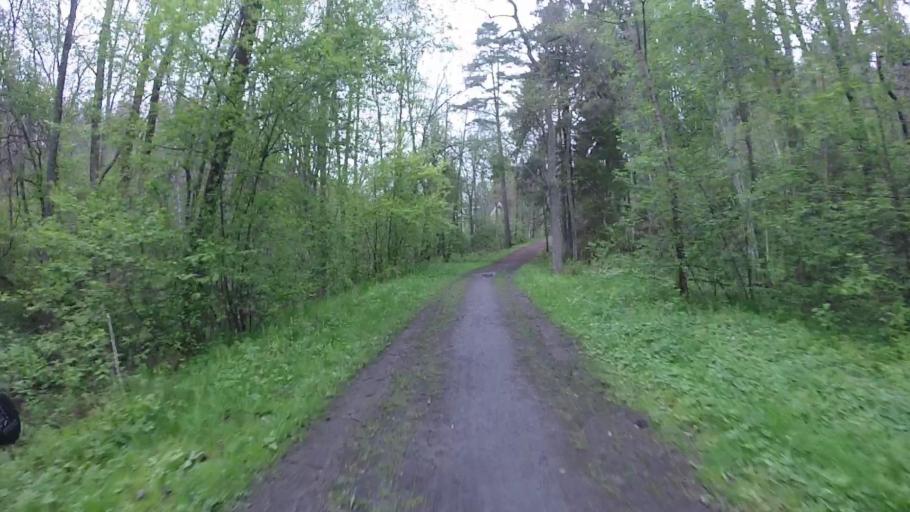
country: SE
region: Vaestra Goetaland
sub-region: Trollhattan
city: Trollhattan
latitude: 58.2588
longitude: 12.2526
